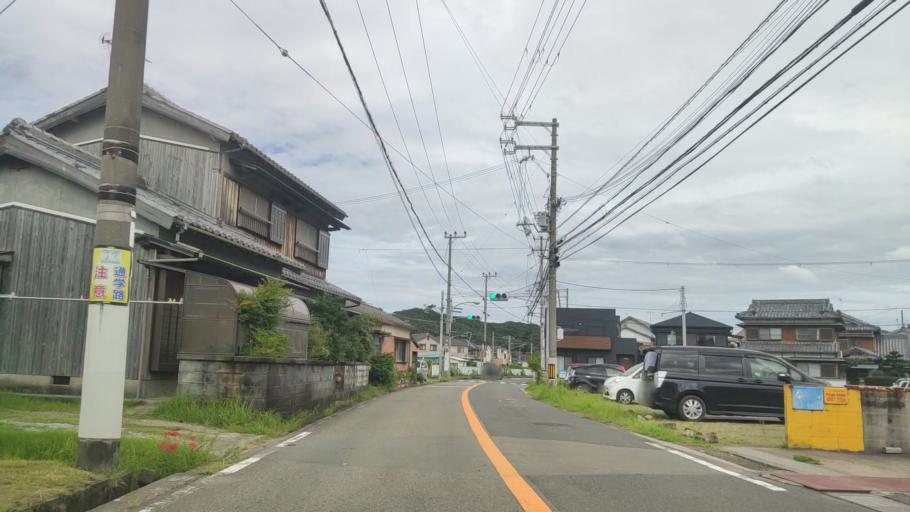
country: JP
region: Wakayama
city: Tanabe
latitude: 33.6636
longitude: 135.3855
